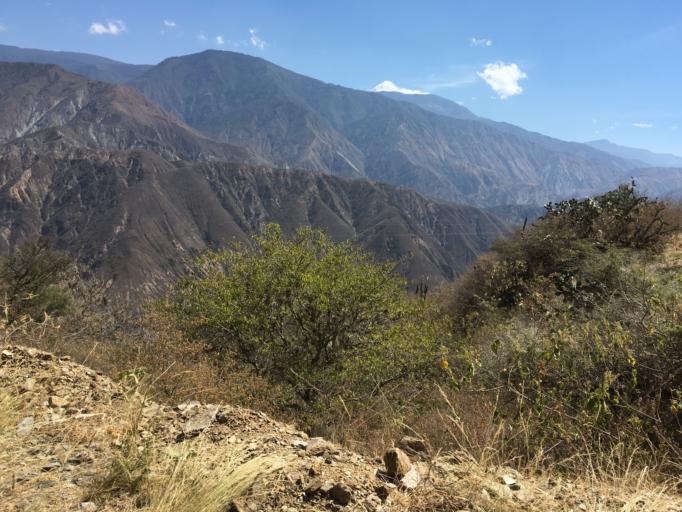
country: CO
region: Santander
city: Aratoca
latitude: 6.7837
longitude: -72.9962
